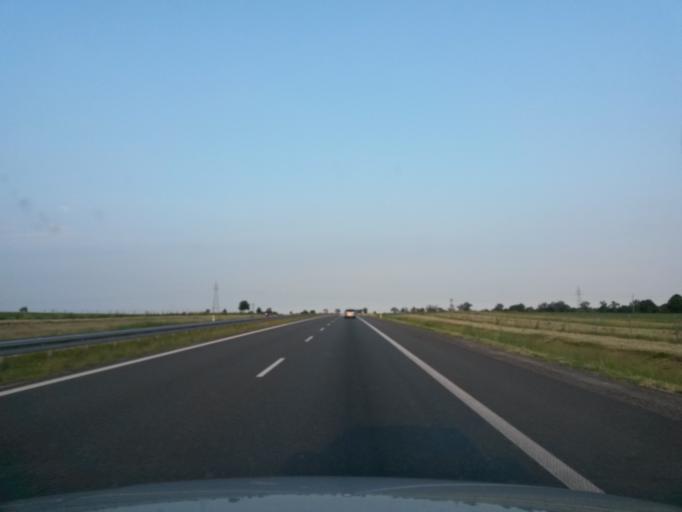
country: PL
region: Lower Silesian Voivodeship
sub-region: Powiat olesnicki
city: Sycow
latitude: 51.2984
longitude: 17.6577
